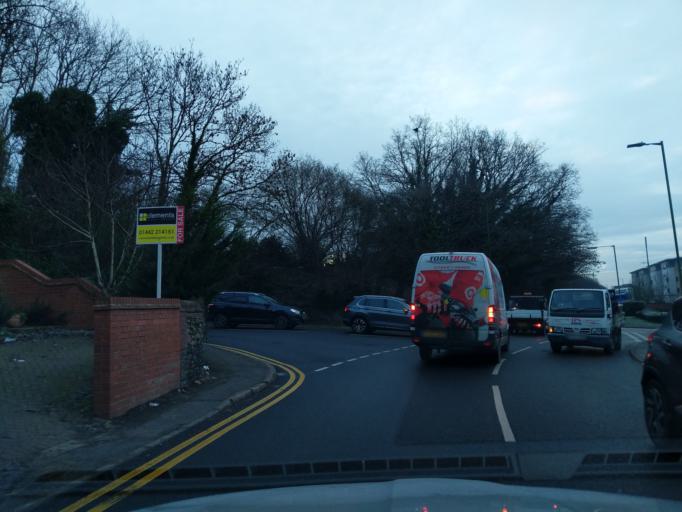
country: GB
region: England
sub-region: Hertfordshire
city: Kings Langley
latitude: 51.7144
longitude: -0.4412
